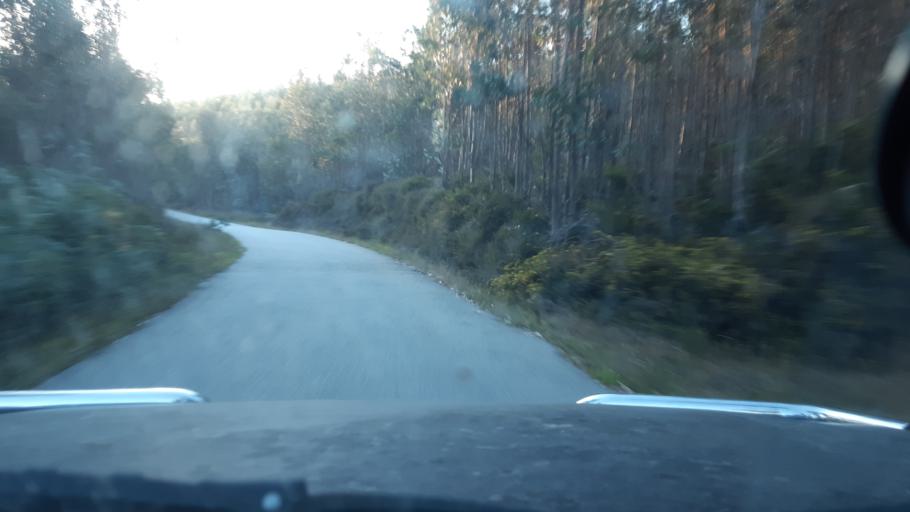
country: PT
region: Aveiro
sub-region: Agueda
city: Aguada de Cima
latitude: 40.5543
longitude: -8.2882
